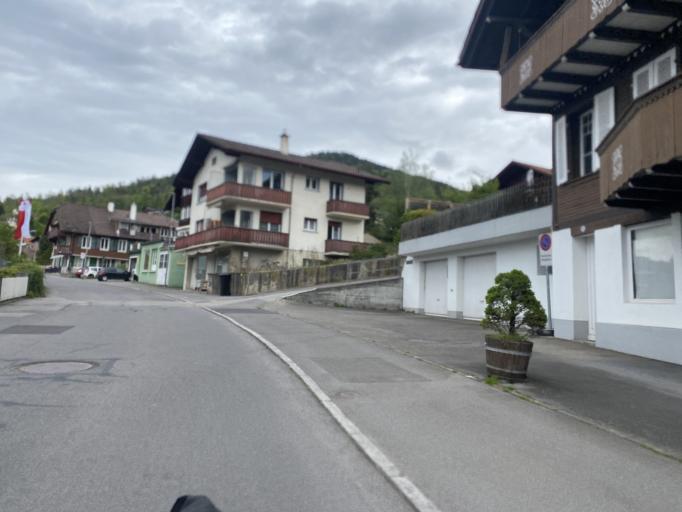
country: CH
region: Bern
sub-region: Thun District
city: Hilterfingen
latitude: 46.7468
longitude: 7.6504
